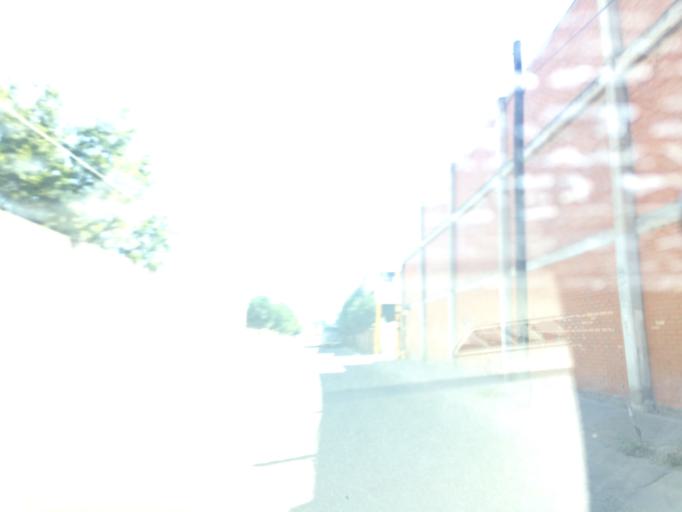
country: MX
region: Guanajuato
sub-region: Leon
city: San Jose de Duran (Los Troncoso)
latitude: 21.0892
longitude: -101.6644
